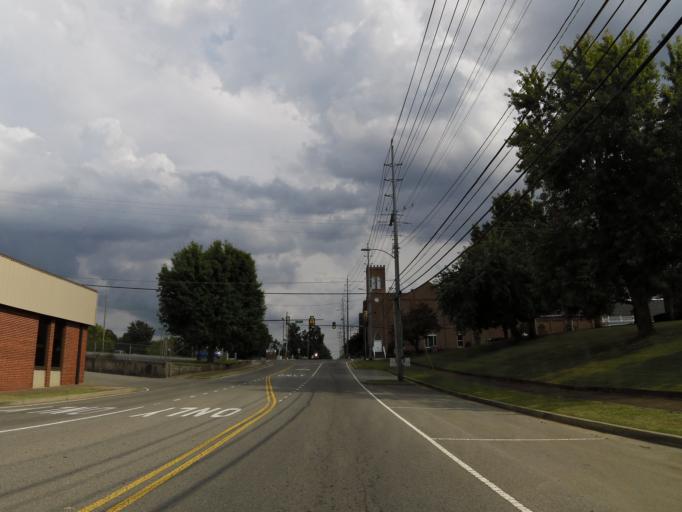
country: US
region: Tennessee
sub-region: Dickson County
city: Dickson
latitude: 36.0746
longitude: -87.3903
